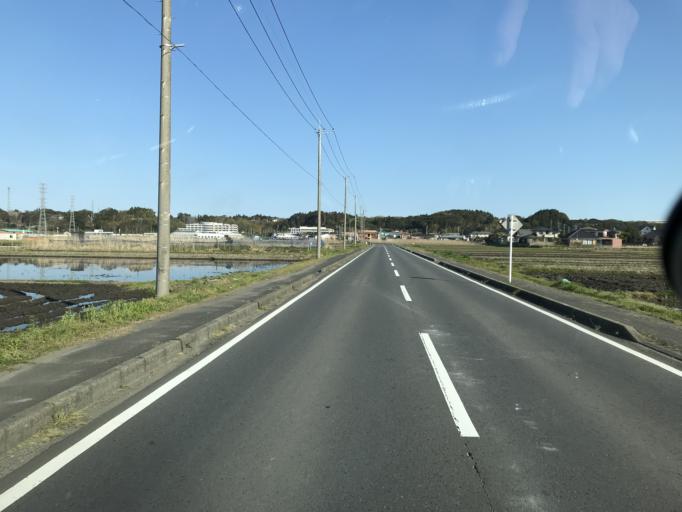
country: JP
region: Chiba
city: Omigawa
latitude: 35.8475
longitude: 140.5909
